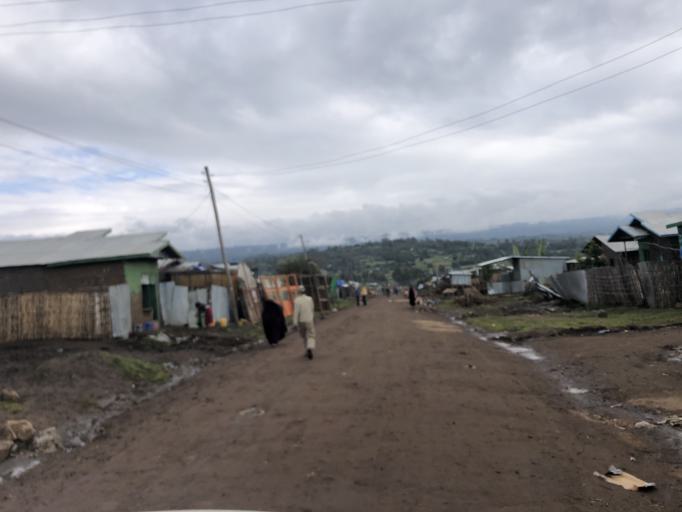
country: ET
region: Southern Nations, Nationalities, and People's Region
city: Butajira
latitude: 7.8382
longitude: 38.1738
